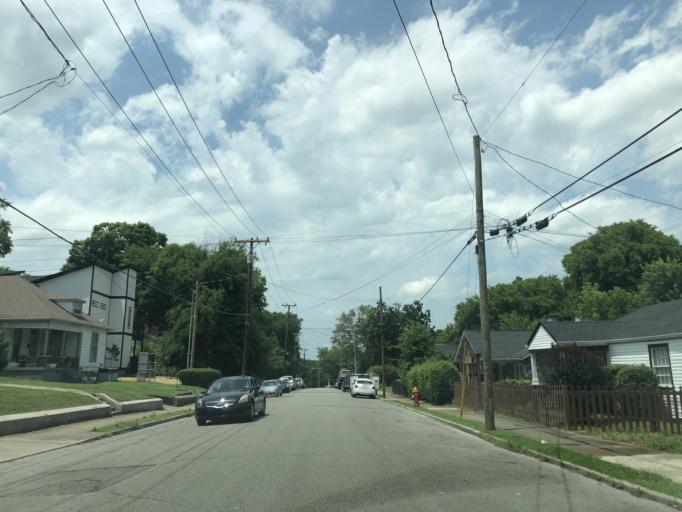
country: US
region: Tennessee
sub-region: Davidson County
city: Nashville
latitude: 36.1781
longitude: -86.7574
